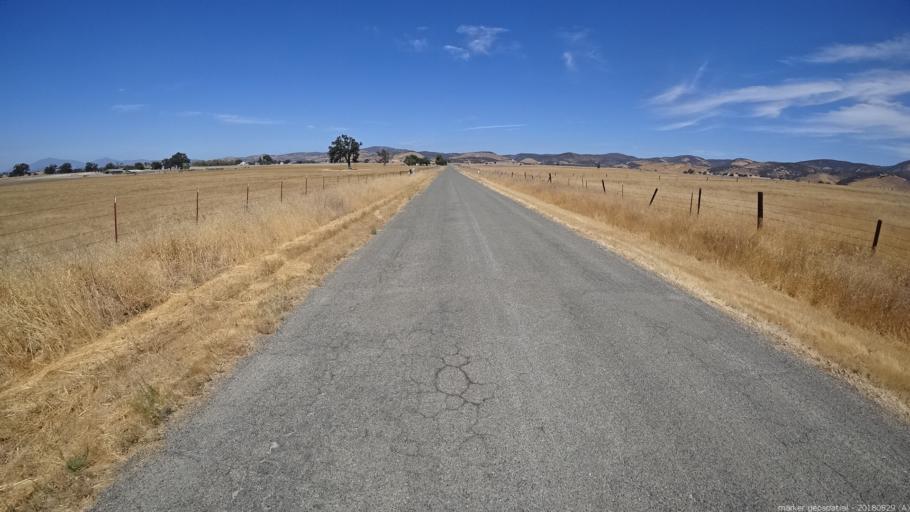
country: US
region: California
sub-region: San Luis Obispo County
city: Lake Nacimiento
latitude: 35.9286
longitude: -121.0643
